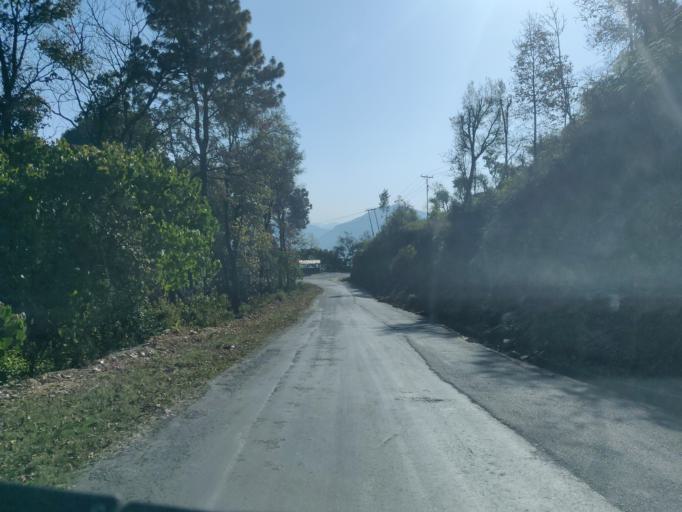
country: NP
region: Western Region
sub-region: Gandaki Zone
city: Pokhara
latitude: 28.2448
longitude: 83.9626
